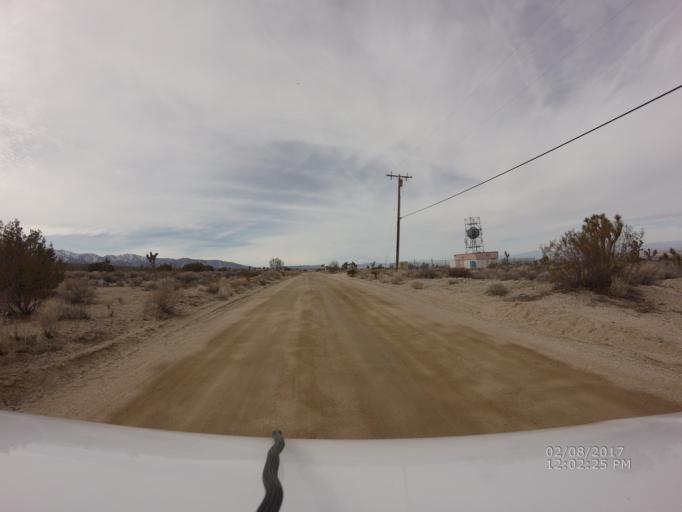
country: US
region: California
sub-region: San Bernardino County
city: Pinon Hills
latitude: 34.4695
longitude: -117.7672
